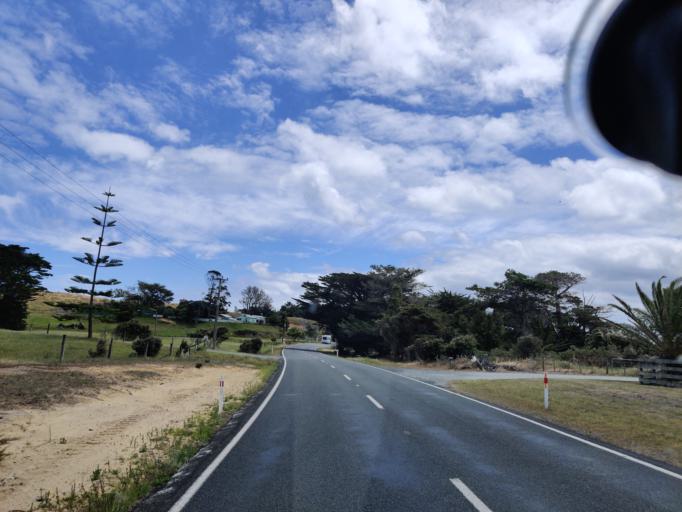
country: NZ
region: Northland
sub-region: Far North District
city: Kaitaia
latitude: -34.7907
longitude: 173.1014
